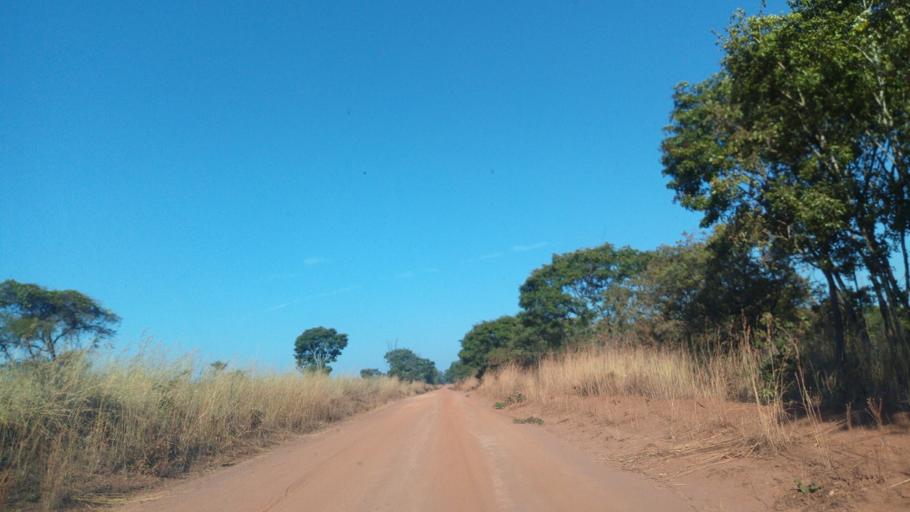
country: ZM
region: Luapula
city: Mwense
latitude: -10.5978
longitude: 28.4284
